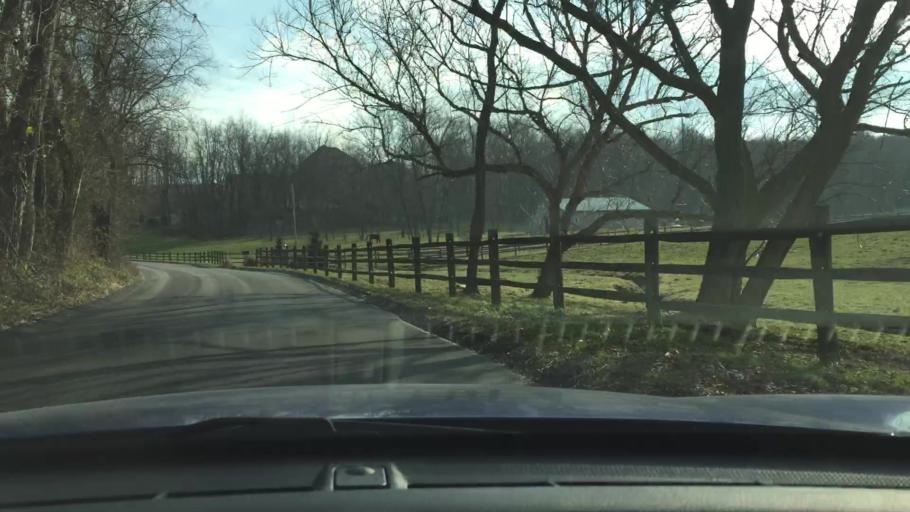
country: US
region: Pennsylvania
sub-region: Washington County
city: Thompsonville
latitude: 40.2918
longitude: -80.1294
